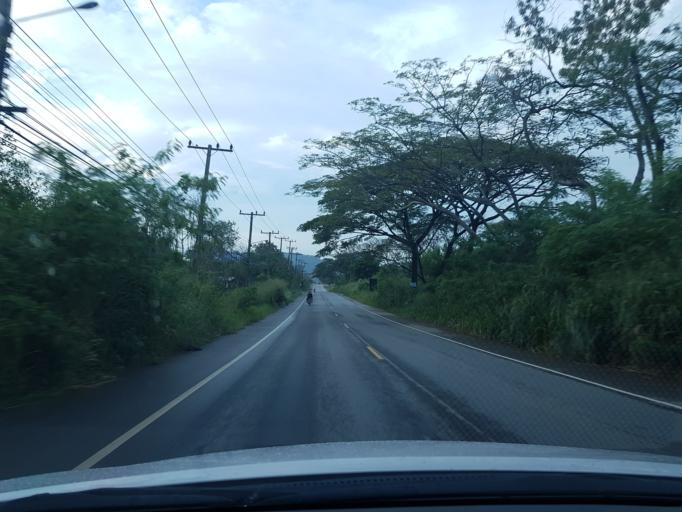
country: TH
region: Sara Buri
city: Muak Lek
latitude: 14.6142
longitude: 101.1930
